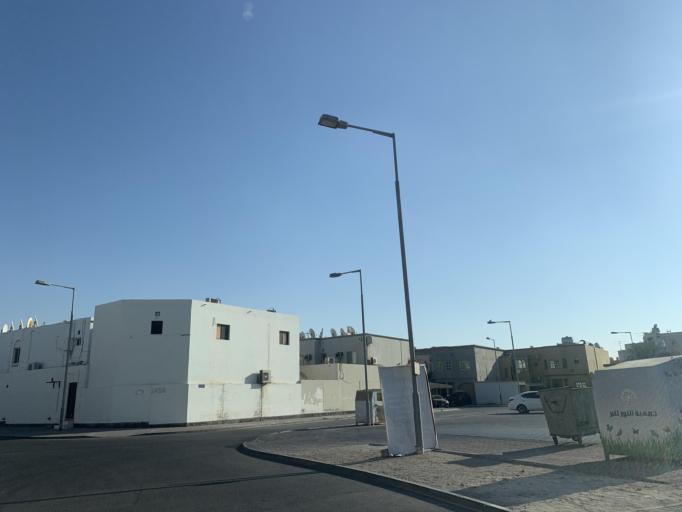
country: BH
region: Central Governorate
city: Madinat Hamad
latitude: 26.1054
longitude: 50.5063
